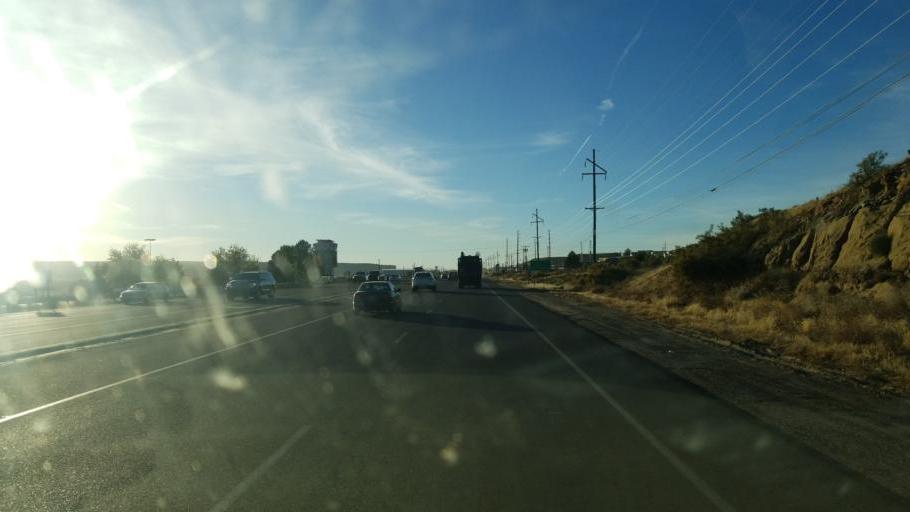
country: US
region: New Mexico
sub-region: San Juan County
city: Lee Acres
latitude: 36.7024
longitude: -108.0958
